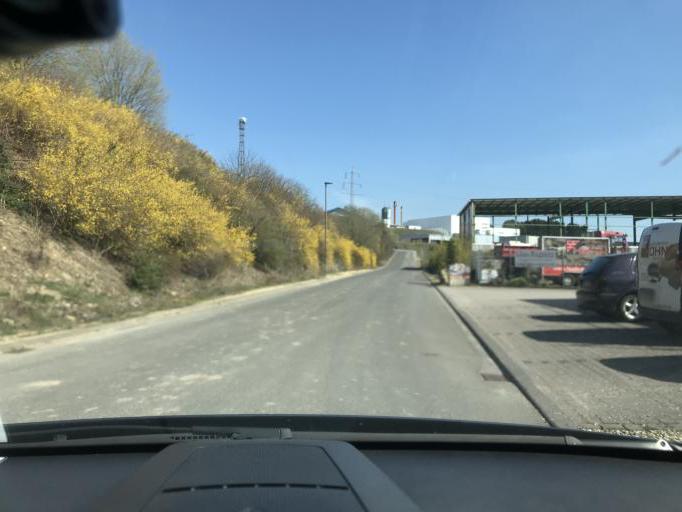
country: DE
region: Rheinland-Pfalz
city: Trierweiler
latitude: 49.7724
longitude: 6.5790
